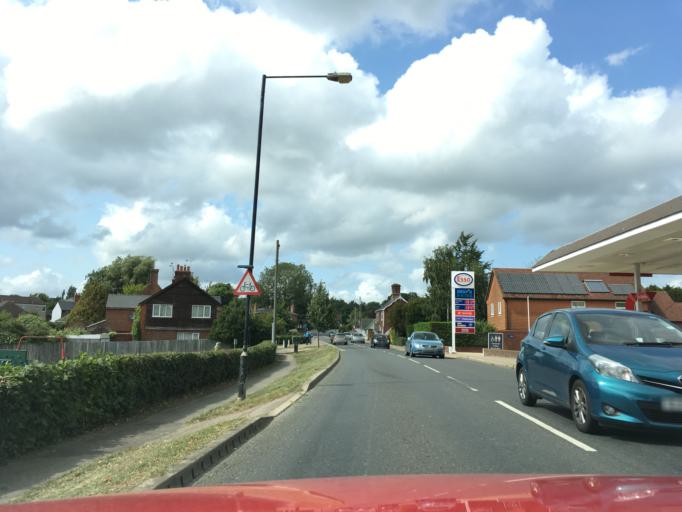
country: GB
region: England
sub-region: Kent
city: Tenterden
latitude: 51.0836
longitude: 0.6928
